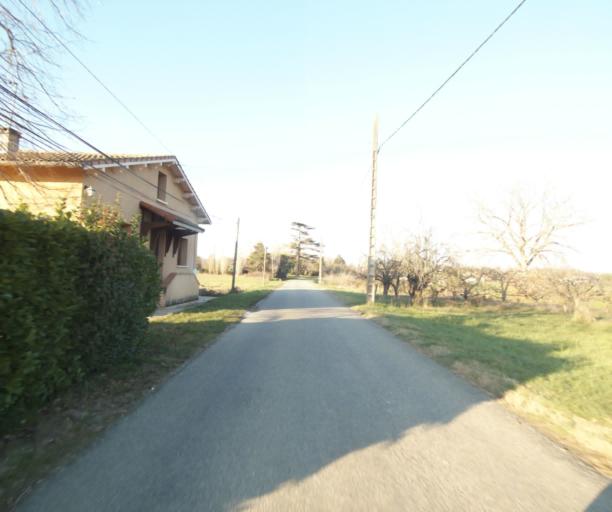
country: FR
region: Midi-Pyrenees
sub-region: Departement du Tarn-et-Garonne
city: Moissac
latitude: 44.1461
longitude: 1.1223
